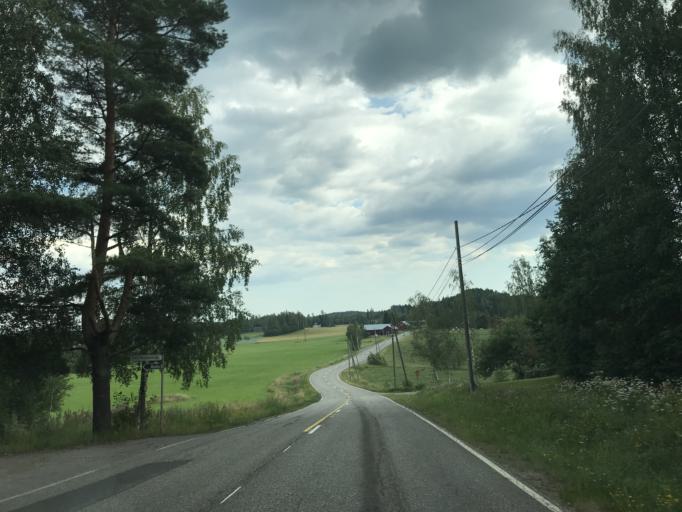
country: FI
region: Uusimaa
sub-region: Helsinki
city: Vihti
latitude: 60.3889
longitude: 24.3441
